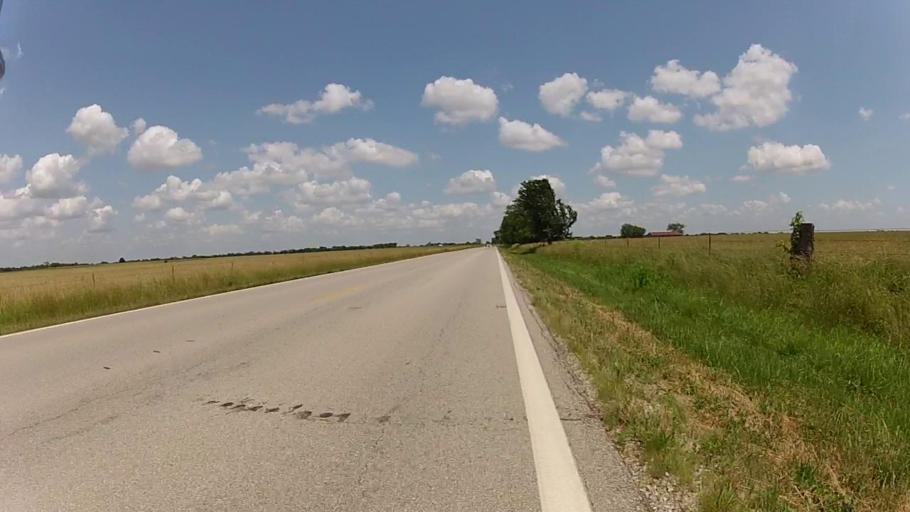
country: US
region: Kansas
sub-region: Labette County
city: Altamont
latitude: 37.1925
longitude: -95.3640
